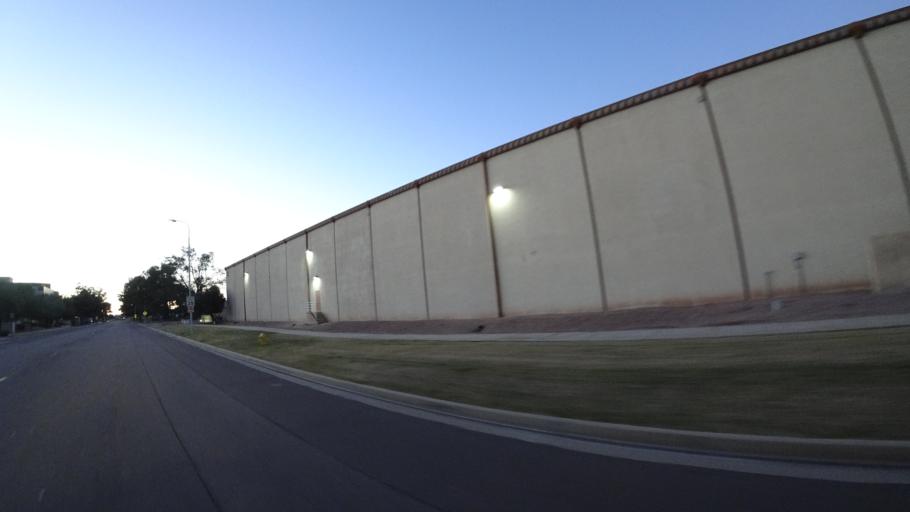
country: US
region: Arizona
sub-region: Maricopa County
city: Tempe Junction
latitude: 33.4136
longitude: -111.9724
